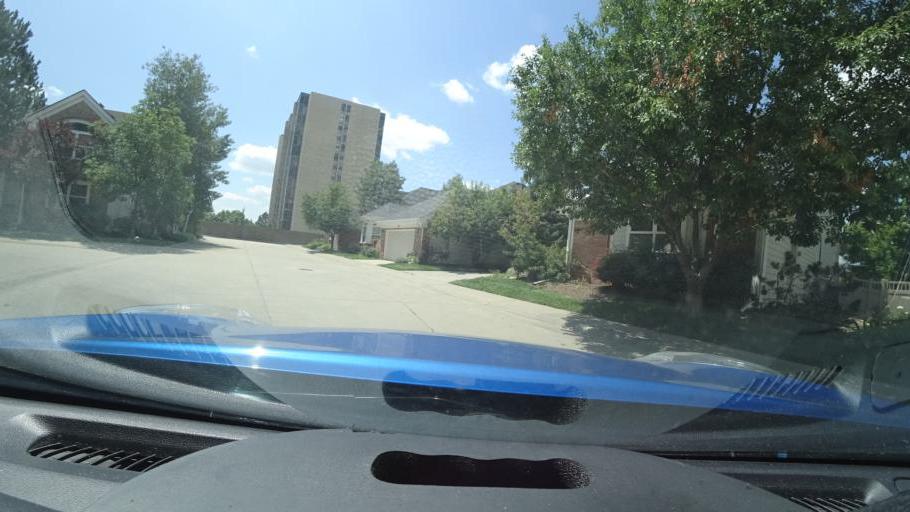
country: US
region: Colorado
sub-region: Arapahoe County
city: Glendale
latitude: 39.6990
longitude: -104.8976
